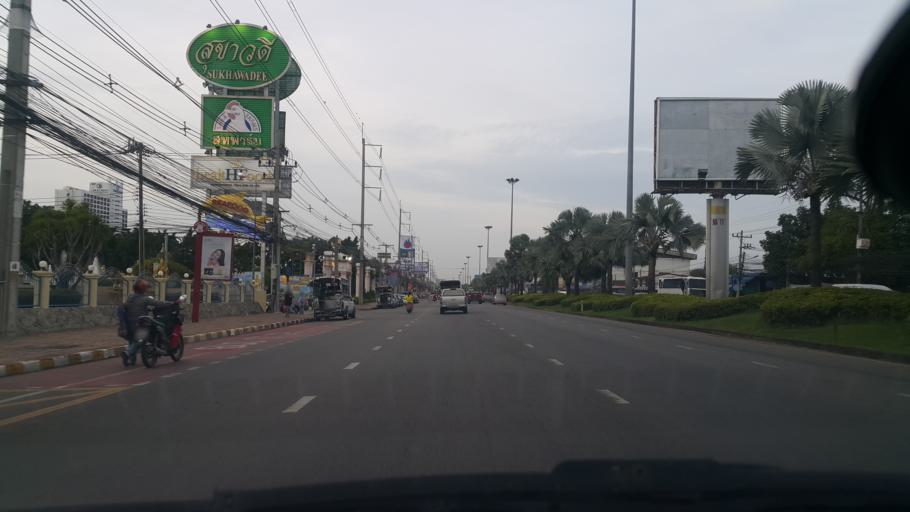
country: TH
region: Chon Buri
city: Phatthaya
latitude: 12.9766
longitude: 100.9150
